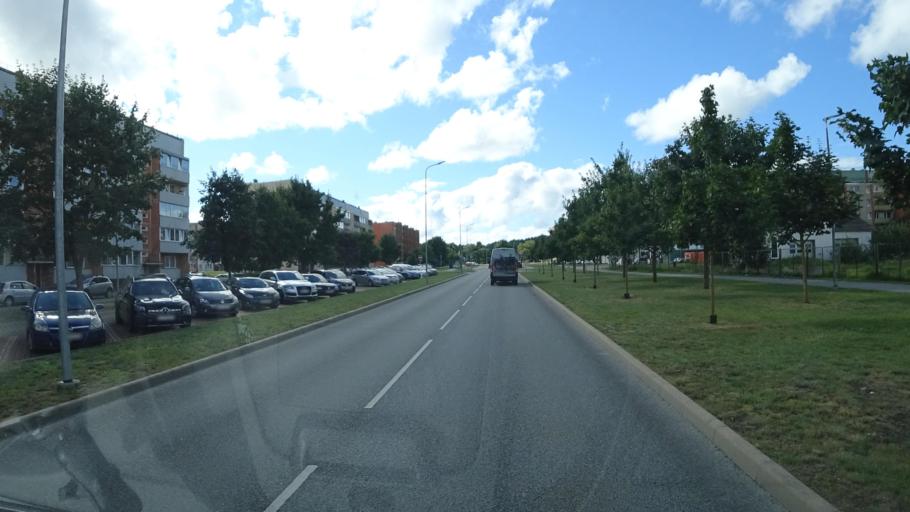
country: LV
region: Ventspils
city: Ventspils
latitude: 57.4075
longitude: 21.5987
